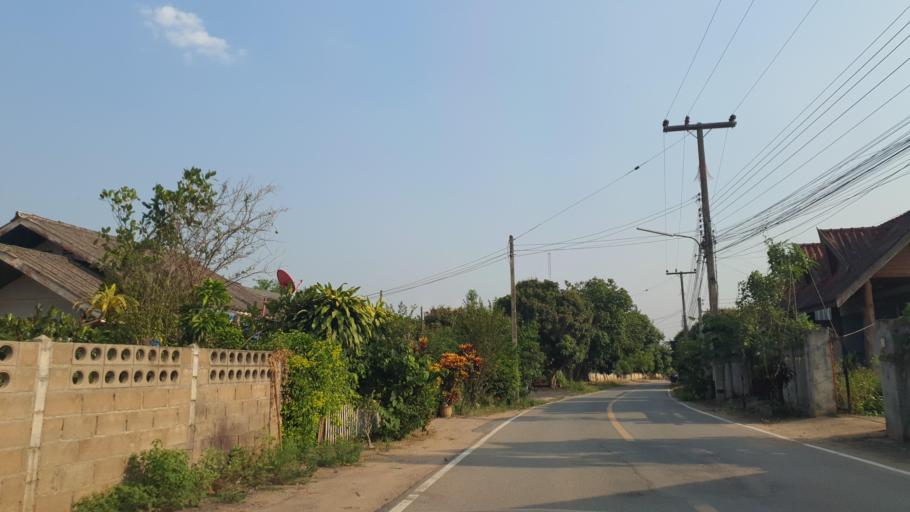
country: TH
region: Chiang Mai
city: Mae Wang
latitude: 18.6600
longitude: 98.8188
